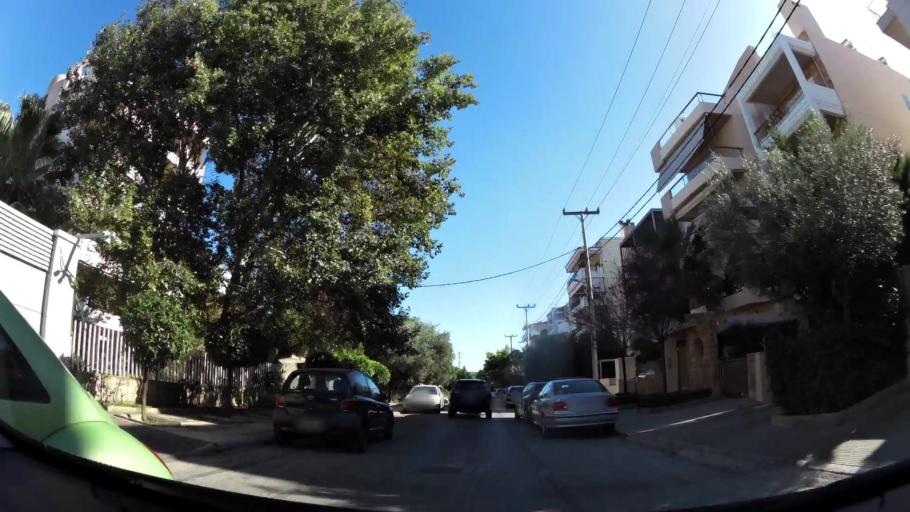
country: GR
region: Attica
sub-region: Nomarchia Anatolikis Attikis
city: Voula
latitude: 37.8446
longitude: 23.7648
